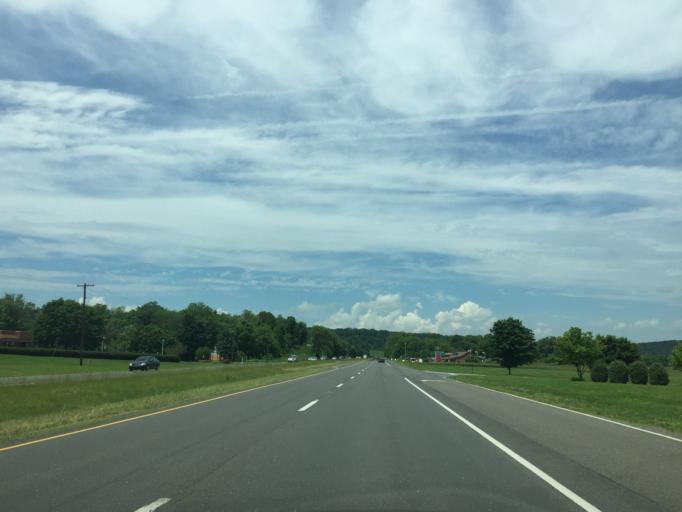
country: US
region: Virginia
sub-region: City of Winchester
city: Winchester
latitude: 39.2195
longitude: -78.1944
